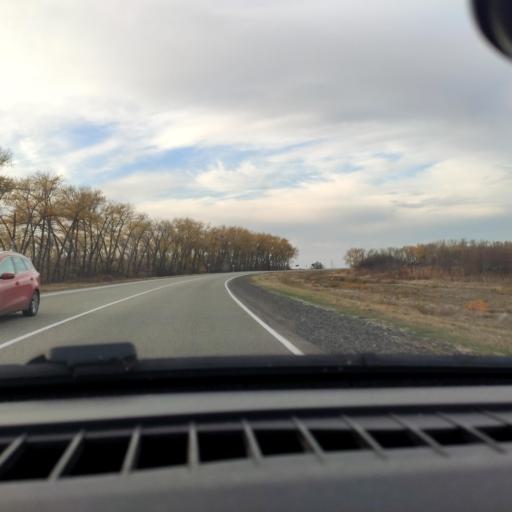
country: RU
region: Voronezj
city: Ostrogozhsk
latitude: 50.9735
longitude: 38.9958
